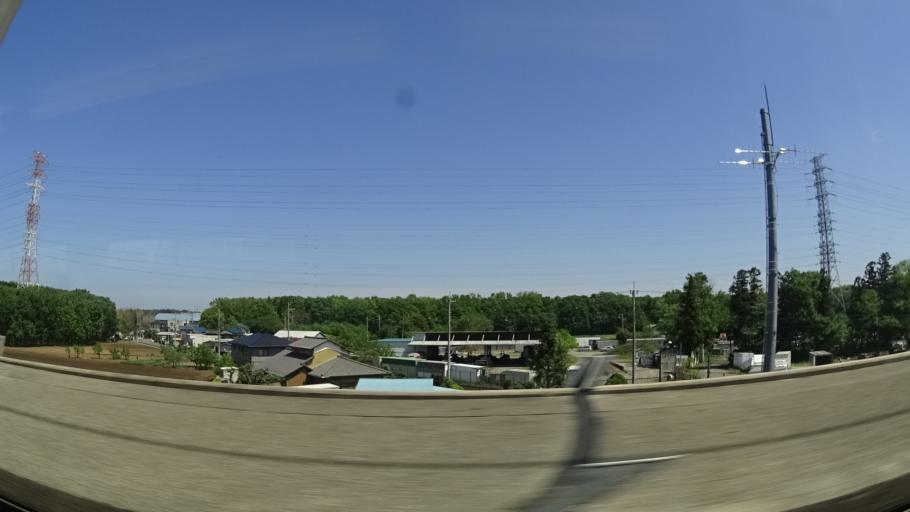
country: JP
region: Tochigi
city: Oyama
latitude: 36.3453
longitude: 139.8251
